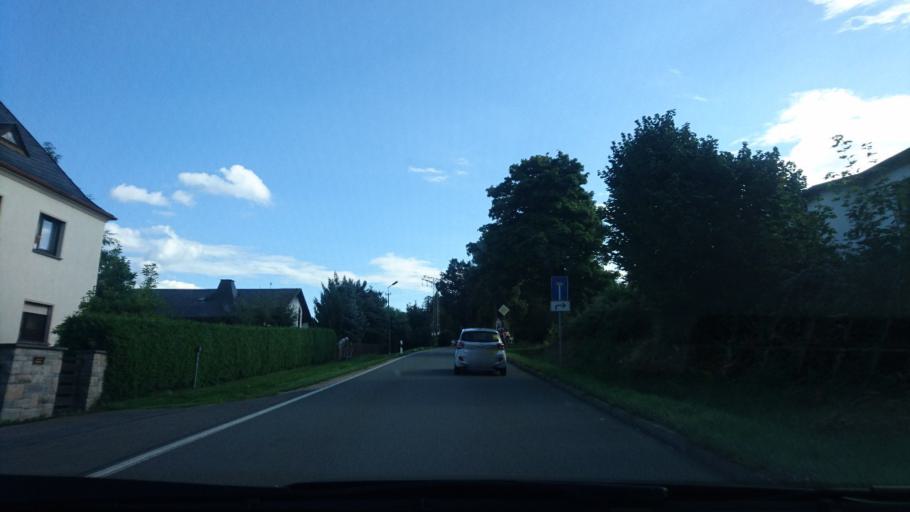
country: DE
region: Saxony
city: Rodewisch
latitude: 50.5209
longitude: 12.4077
